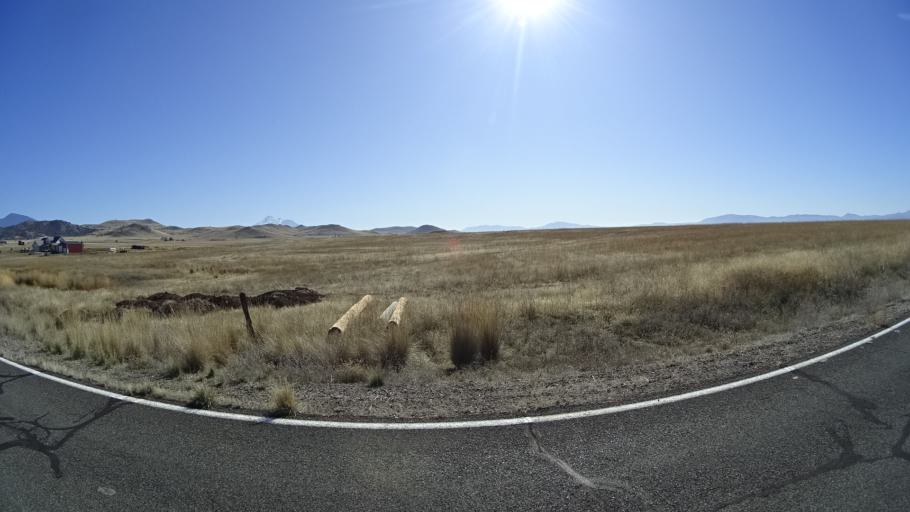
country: US
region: California
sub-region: Siskiyou County
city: Montague
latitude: 41.8081
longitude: -122.4321
